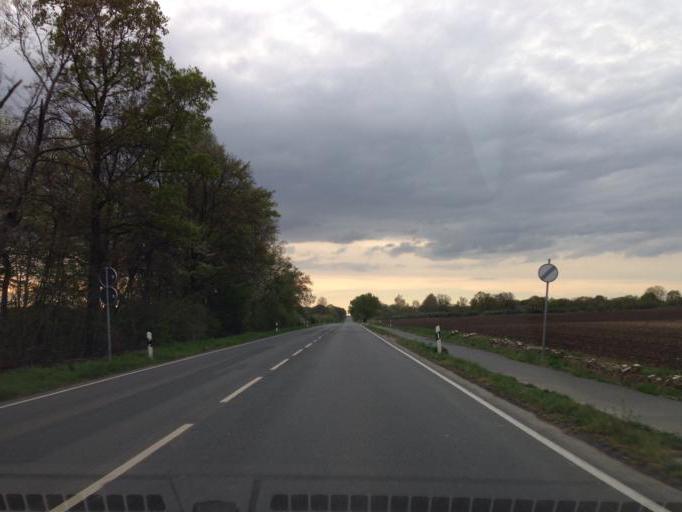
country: DE
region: North Rhine-Westphalia
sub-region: Regierungsbezirk Munster
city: Altenberge
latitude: 52.0233
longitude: 7.4959
